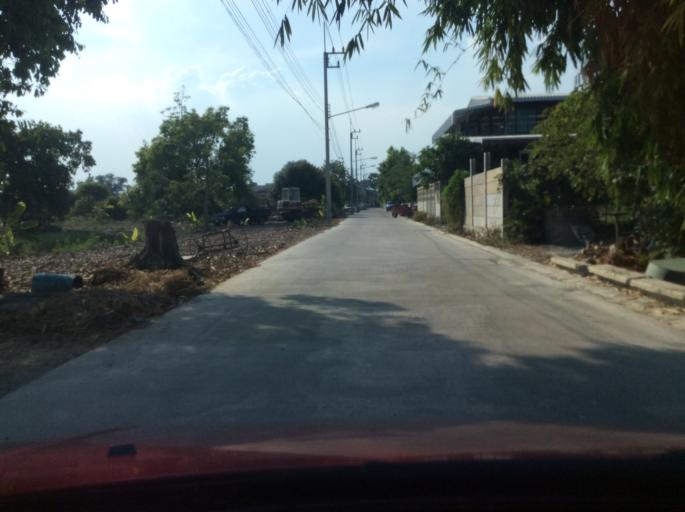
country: TH
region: Pathum Thani
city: Lam Luk Ka
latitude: 13.9677
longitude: 100.7302
